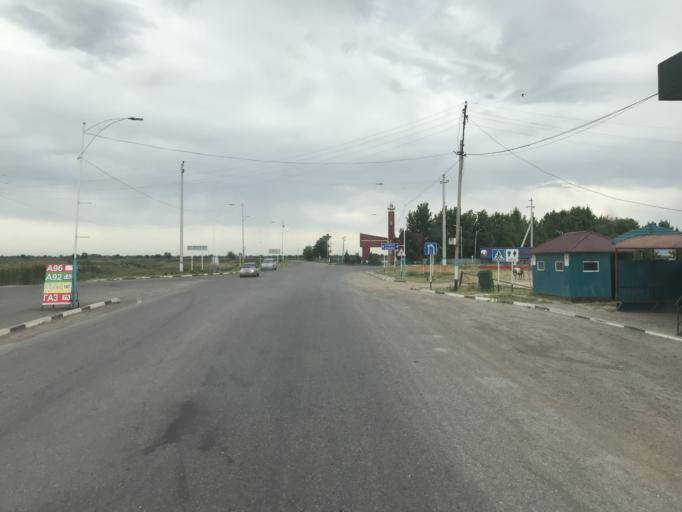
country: KZ
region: Ongtustik Qazaqstan
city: Asykata
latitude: 40.9575
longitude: 68.4636
